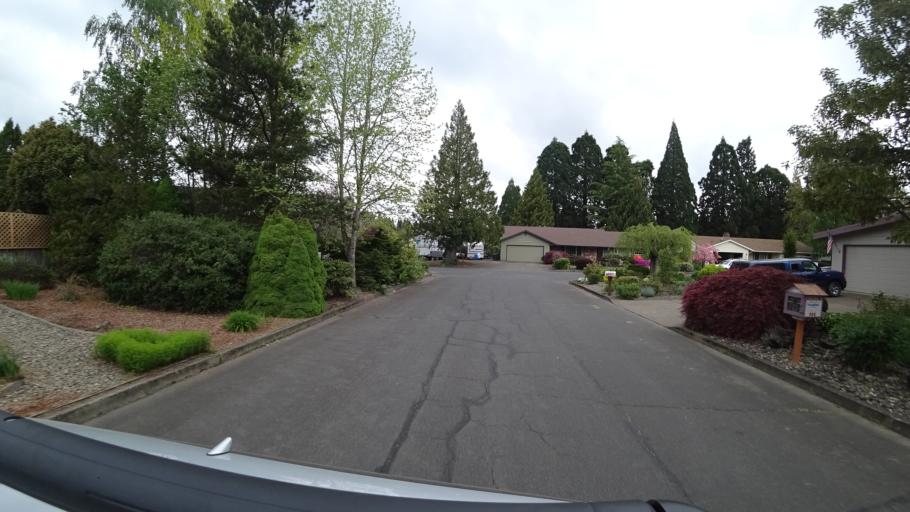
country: US
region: Oregon
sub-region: Washington County
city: Hillsboro
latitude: 45.5308
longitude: -122.9823
